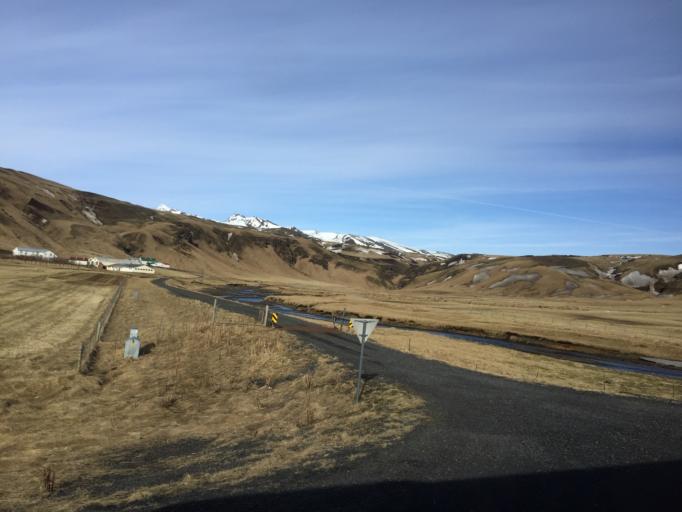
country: IS
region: South
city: Vestmannaeyjar
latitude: 63.4549
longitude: -19.0666
